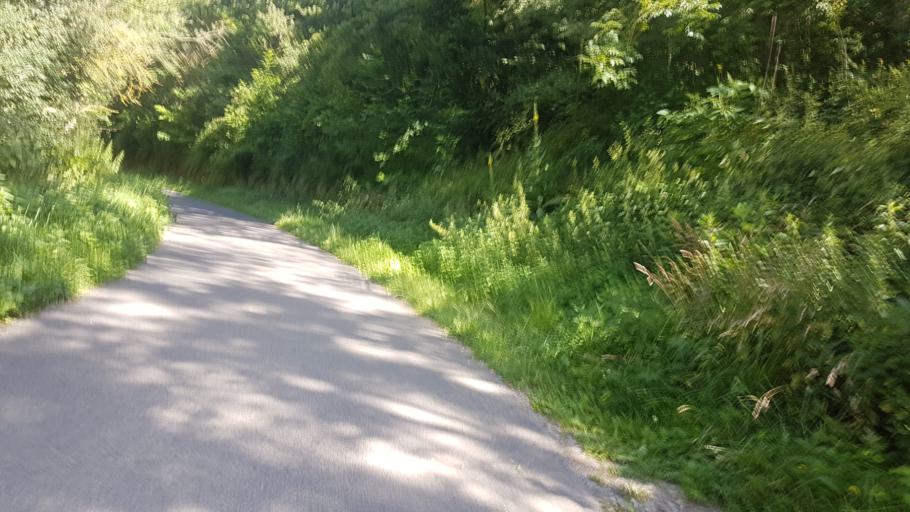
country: DE
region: Bavaria
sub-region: Regierungsbezirk Unterfranken
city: Bieberehren
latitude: 49.5092
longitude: 10.0181
